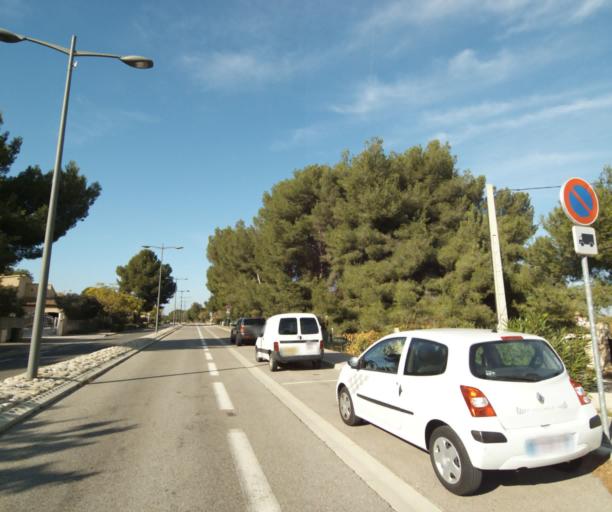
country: FR
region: Provence-Alpes-Cote d'Azur
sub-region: Departement des Bouches-du-Rhone
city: Chateauneuf-les-Martigues
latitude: 43.3763
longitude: 5.1768
